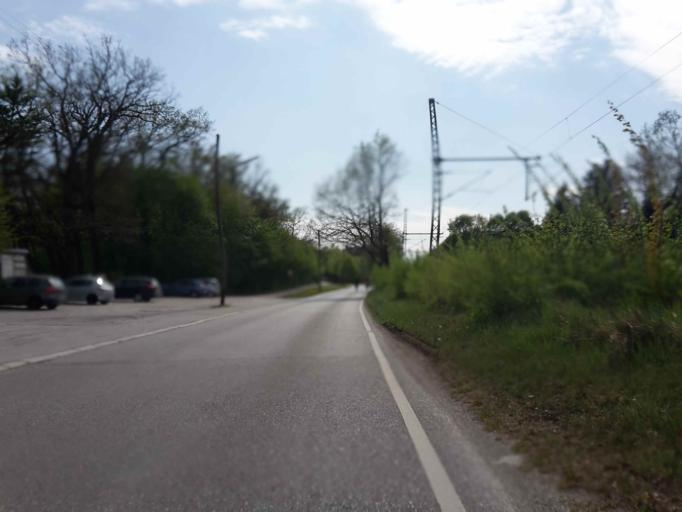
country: DE
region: Bavaria
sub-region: Upper Bavaria
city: Pasing
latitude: 48.1709
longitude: 11.4962
